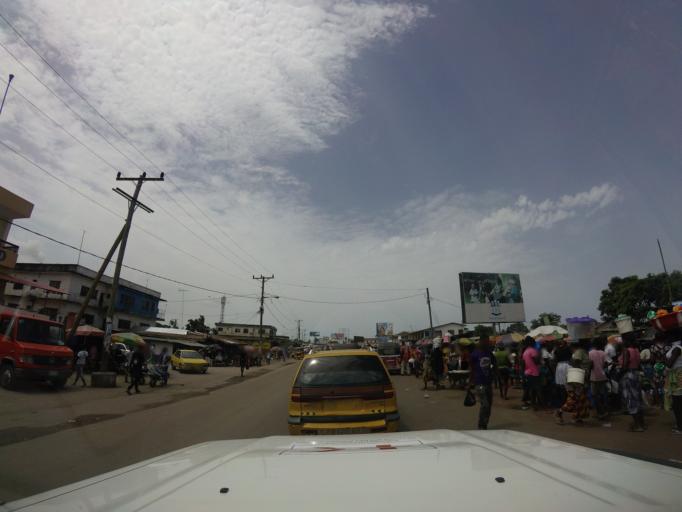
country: LR
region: Montserrado
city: Monrovia
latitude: 6.3743
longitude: -10.7869
